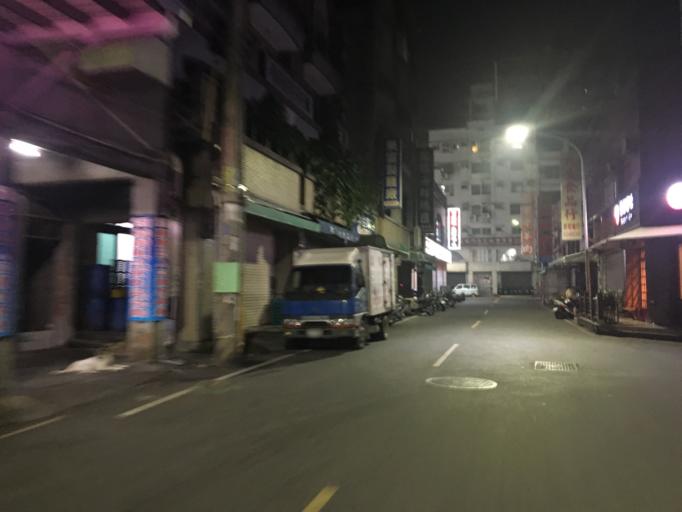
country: TW
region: Taiwan
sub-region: Hsinchu
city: Hsinchu
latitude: 24.8137
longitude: 120.9786
